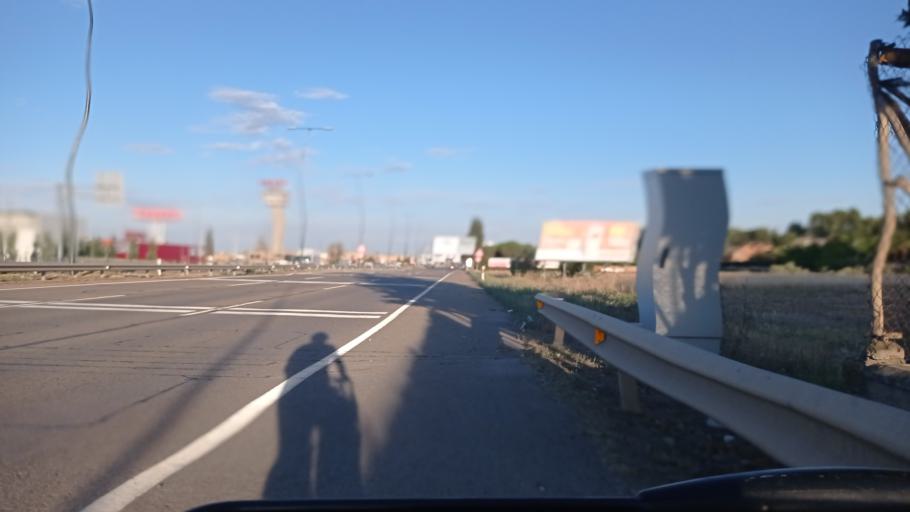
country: ES
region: Aragon
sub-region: Provincia de Zaragoza
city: Oliver-Valdefierro, Oliver, Valdefierro
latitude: 41.6752
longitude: -0.9556
